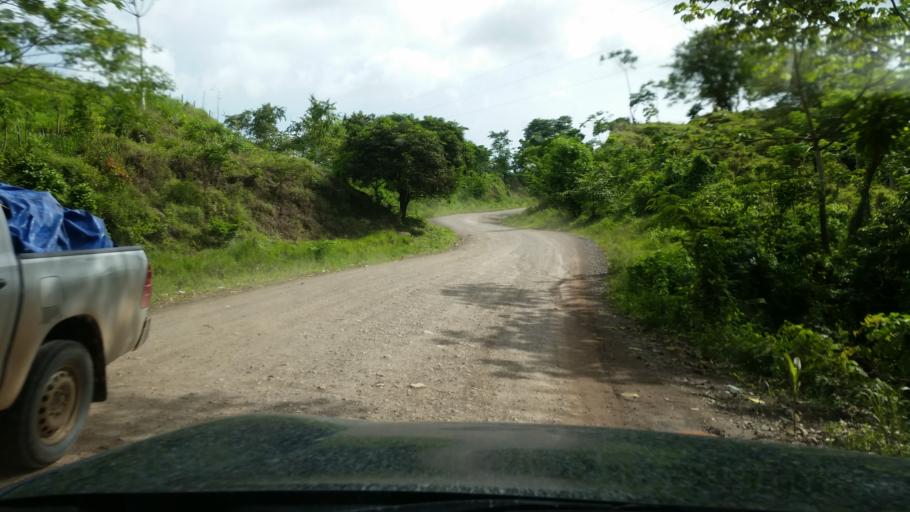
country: NI
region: Atlantico Norte (RAAN)
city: Siuna
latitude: 13.5943
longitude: -84.8067
